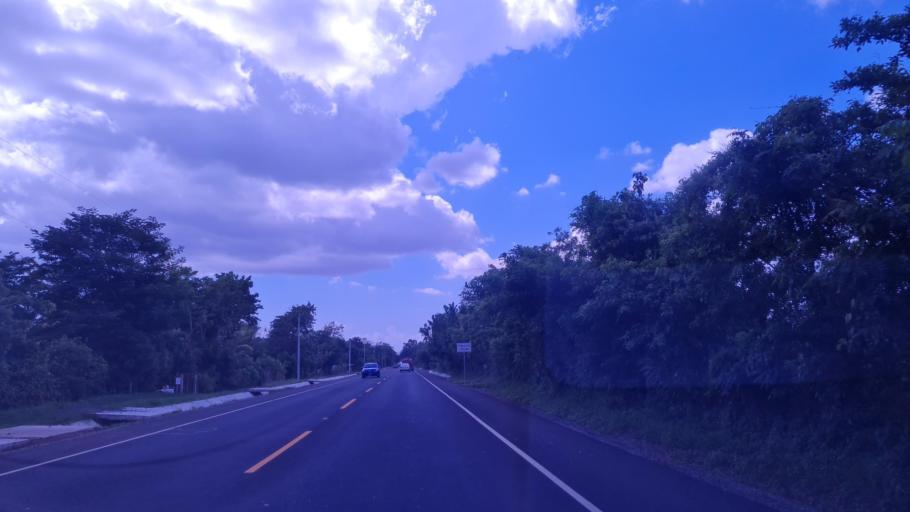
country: NI
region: Masaya
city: Nindiri
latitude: 12.0332
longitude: -86.1252
